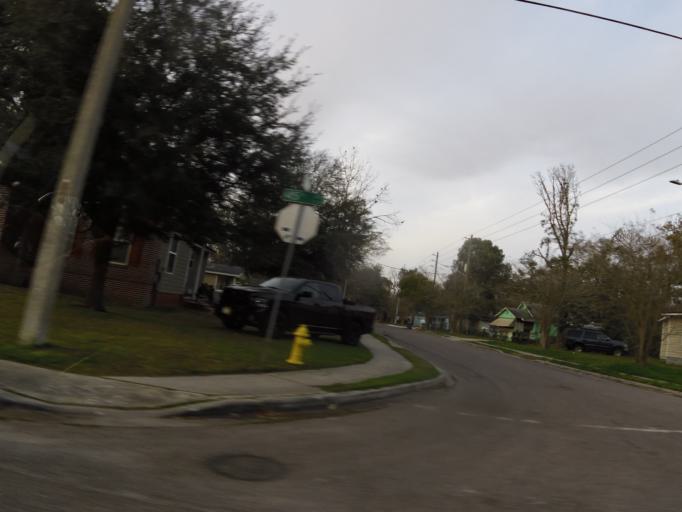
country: US
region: Florida
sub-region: Duval County
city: Jacksonville
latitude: 30.3716
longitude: -81.6982
